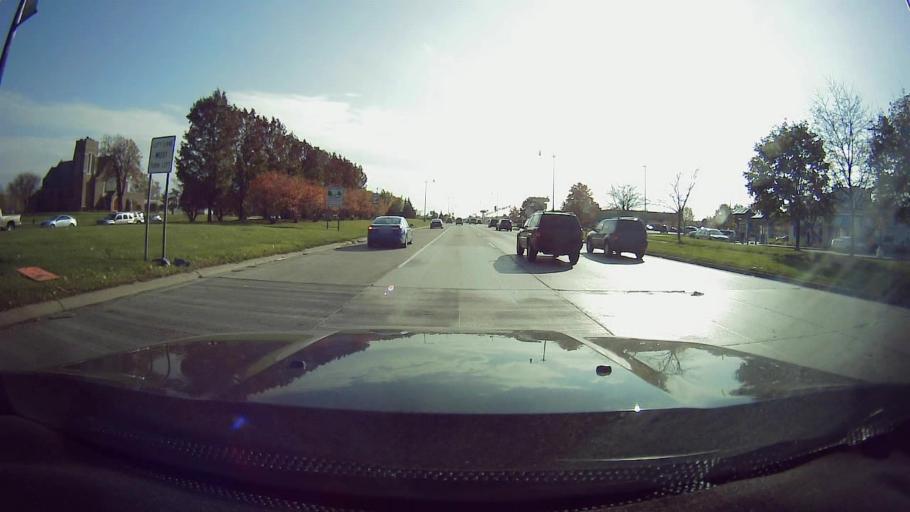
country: US
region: Michigan
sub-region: Wayne County
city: Taylor
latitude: 42.2118
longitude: -83.2689
